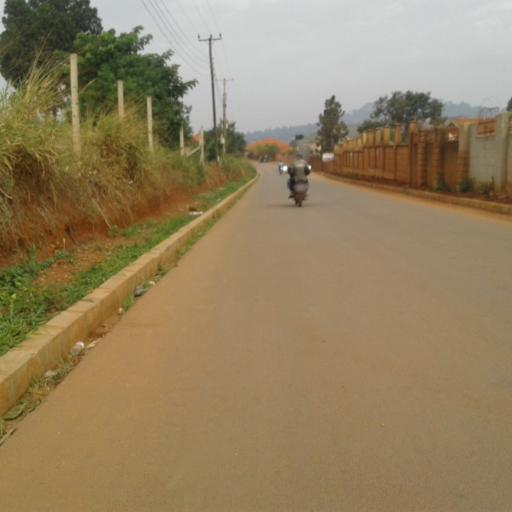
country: UG
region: Central Region
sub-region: Kampala District
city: Kampala
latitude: 0.2764
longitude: 32.6250
